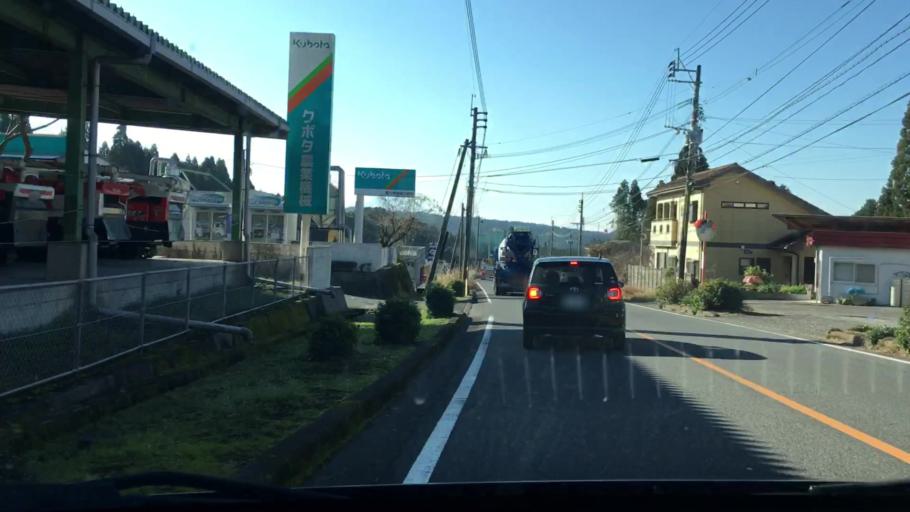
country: JP
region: Kagoshima
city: Kajiki
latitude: 31.7758
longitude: 130.7008
